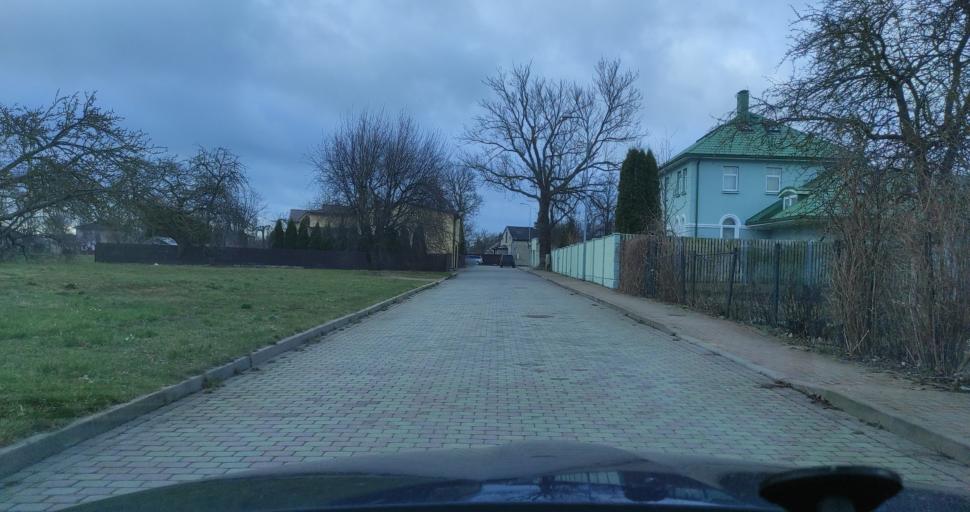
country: LV
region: Ventspils
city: Ventspils
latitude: 57.3825
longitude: 21.5698
